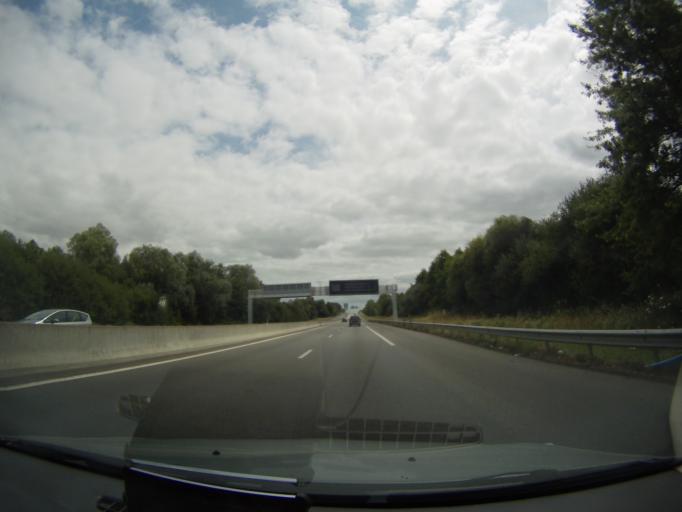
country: FR
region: Pays de la Loire
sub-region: Departement de la Loire-Atlantique
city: Sainte-Luce-sur-Loire
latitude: 47.2417
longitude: -1.4905
